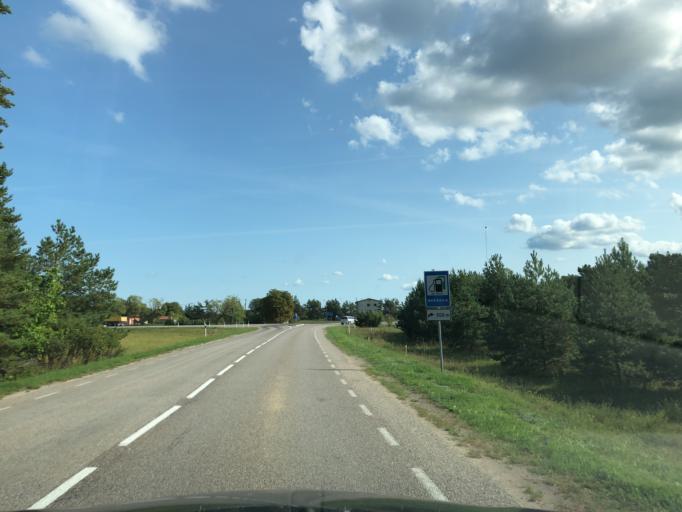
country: EE
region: Hiiumaa
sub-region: Kaerdla linn
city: Kardla
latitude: 58.7064
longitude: 22.5959
